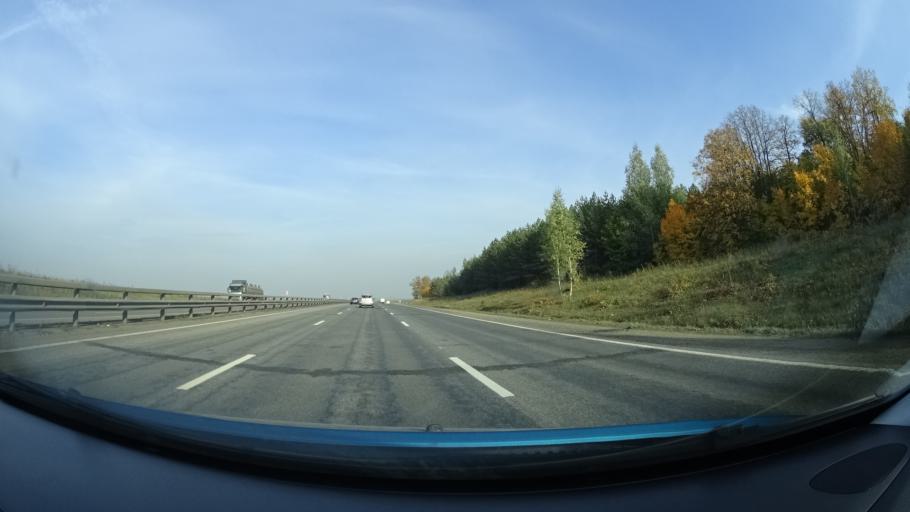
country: RU
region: Bashkortostan
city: Avdon
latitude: 54.6540
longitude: 55.6792
